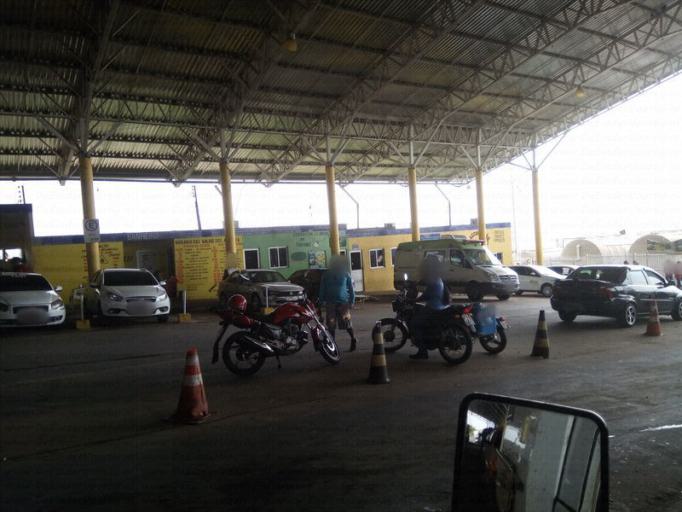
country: BR
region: Amazonas
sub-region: Manaus
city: Manaus
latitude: -3.1350
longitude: -59.9391
